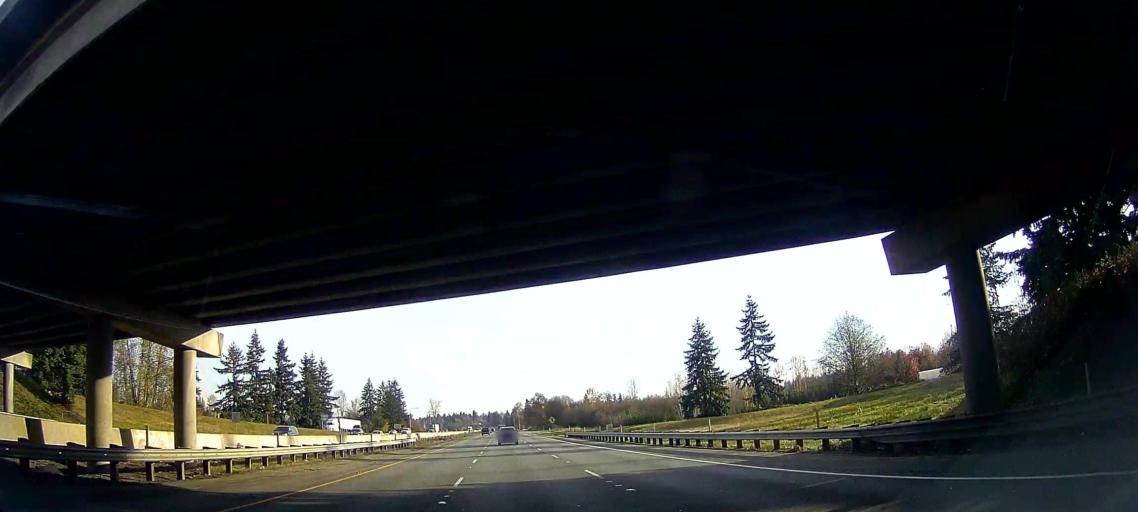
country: US
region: Washington
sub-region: Snohomish County
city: Smokey Point
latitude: 48.1878
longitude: -122.2033
